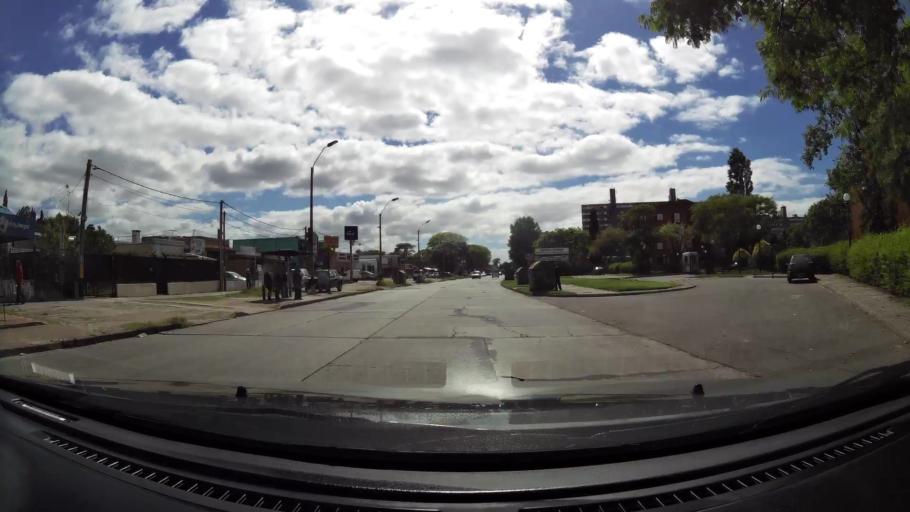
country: UY
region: Canelones
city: Paso de Carrasco
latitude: -34.8723
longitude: -56.1213
